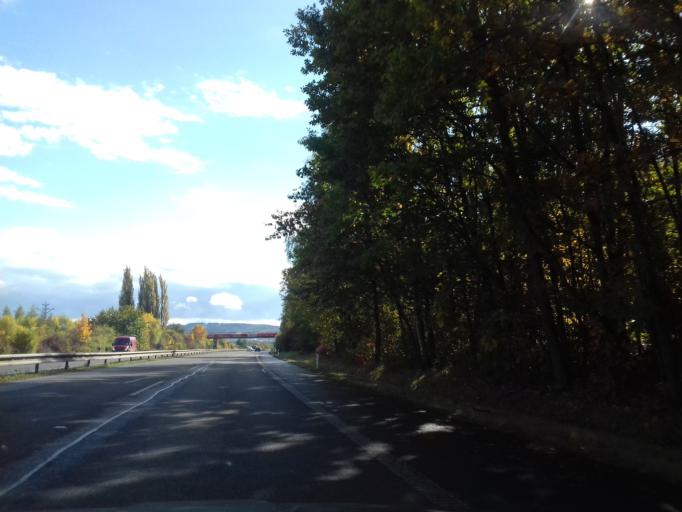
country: CZ
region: Central Bohemia
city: Kosmonosy
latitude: 50.4442
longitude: 14.9412
